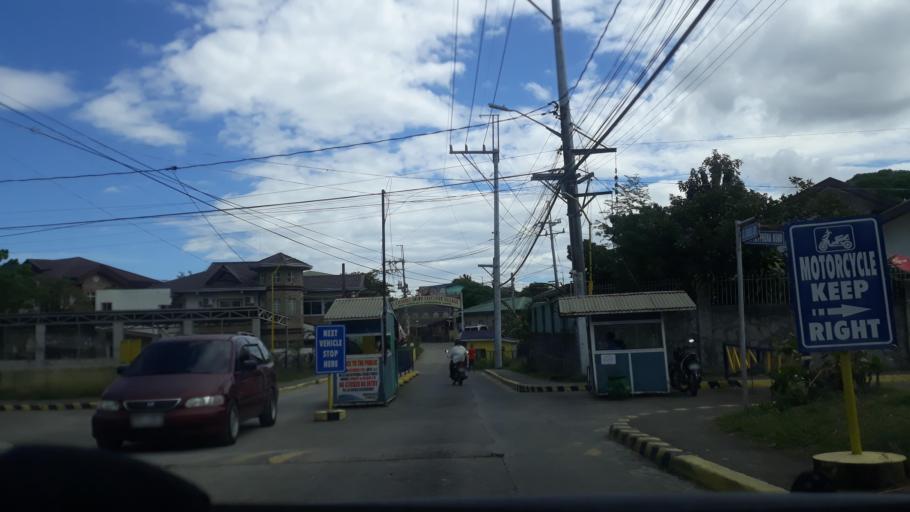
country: PH
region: Calabarzon
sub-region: Province of Cavite
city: Bulihan
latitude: 14.3044
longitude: 120.9709
